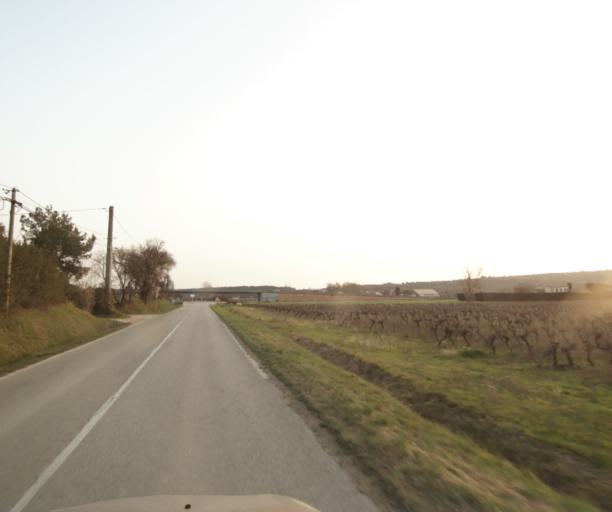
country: FR
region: Provence-Alpes-Cote d'Azur
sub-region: Departement des Bouches-du-Rhone
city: Eguilles
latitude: 43.5462
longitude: 5.3486
